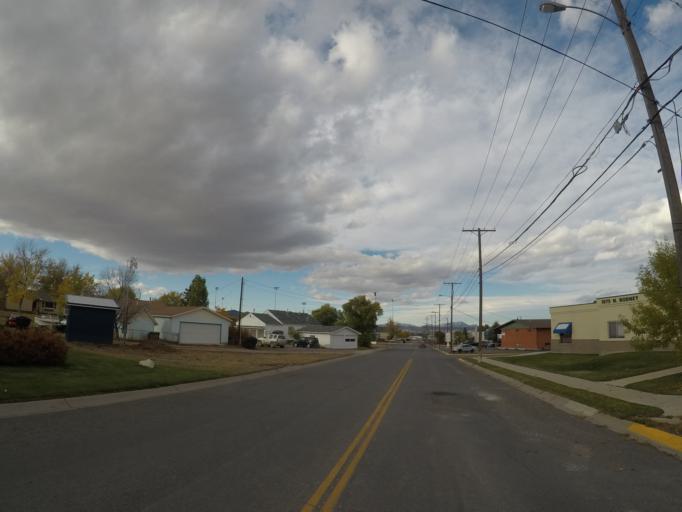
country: US
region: Montana
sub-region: Lewis and Clark County
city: Helena
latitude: 46.5968
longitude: -112.0259
